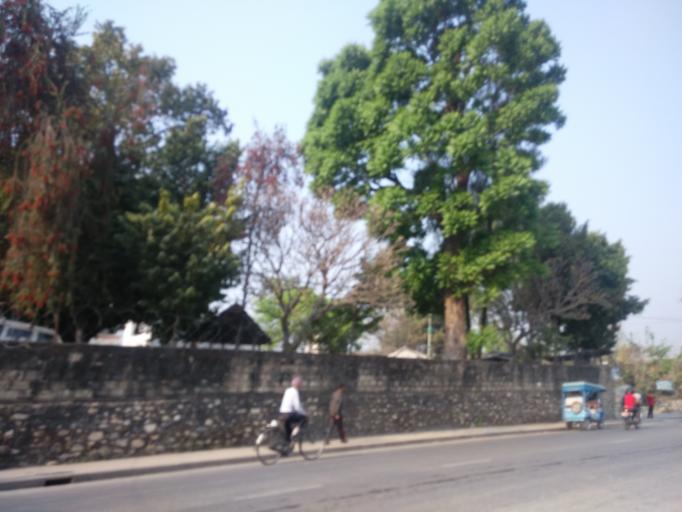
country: NP
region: Central Region
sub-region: Narayani Zone
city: Hitura
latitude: 27.4319
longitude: 85.0288
